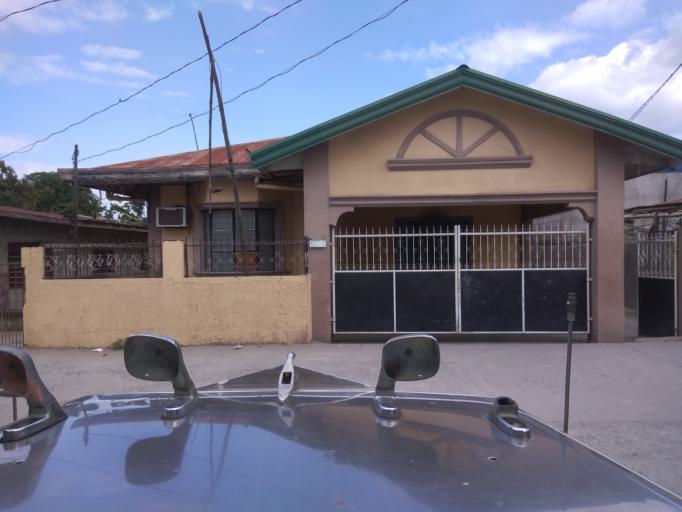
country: PH
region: Central Luzon
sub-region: Province of Pampanga
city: Pandacaqui
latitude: 15.1827
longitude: 120.6472
